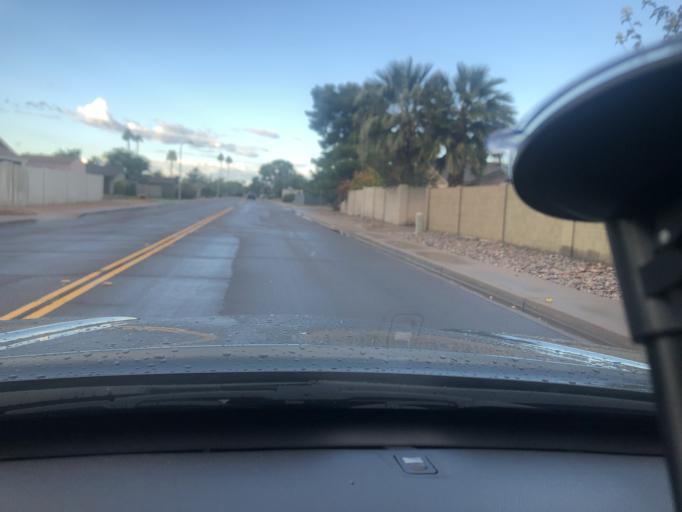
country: US
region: Arizona
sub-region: Maricopa County
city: Scottsdale
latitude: 33.4891
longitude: -111.8938
